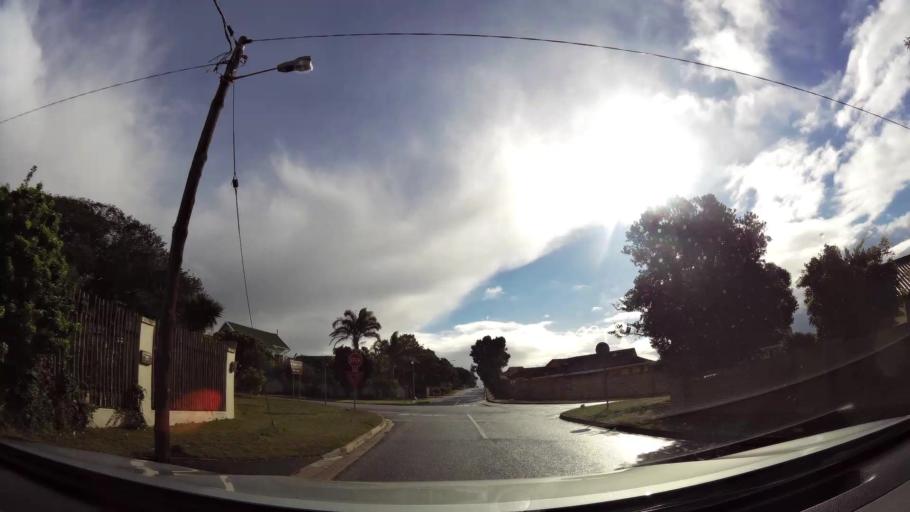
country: ZA
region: Western Cape
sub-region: Eden District Municipality
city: Mossel Bay
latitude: -34.1886
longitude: 22.1321
